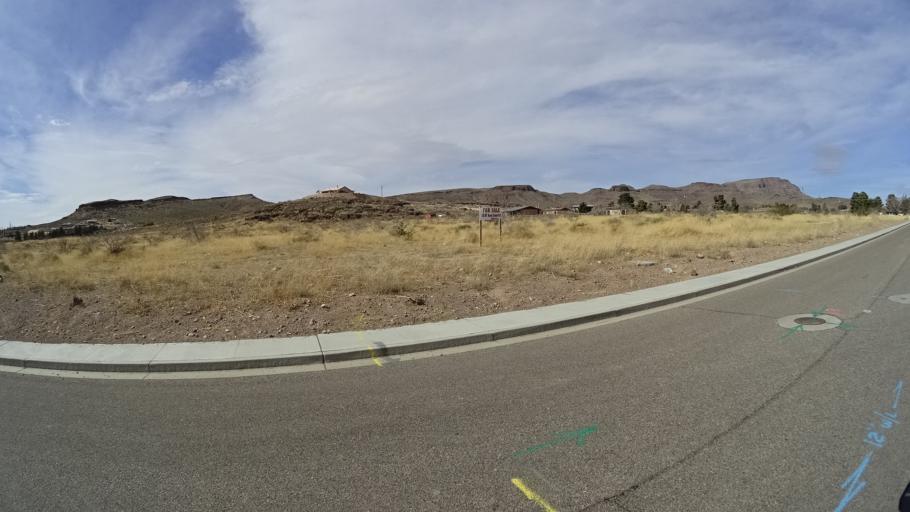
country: US
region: Arizona
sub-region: Mohave County
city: New Kingman-Butler
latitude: 35.2274
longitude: -114.0423
